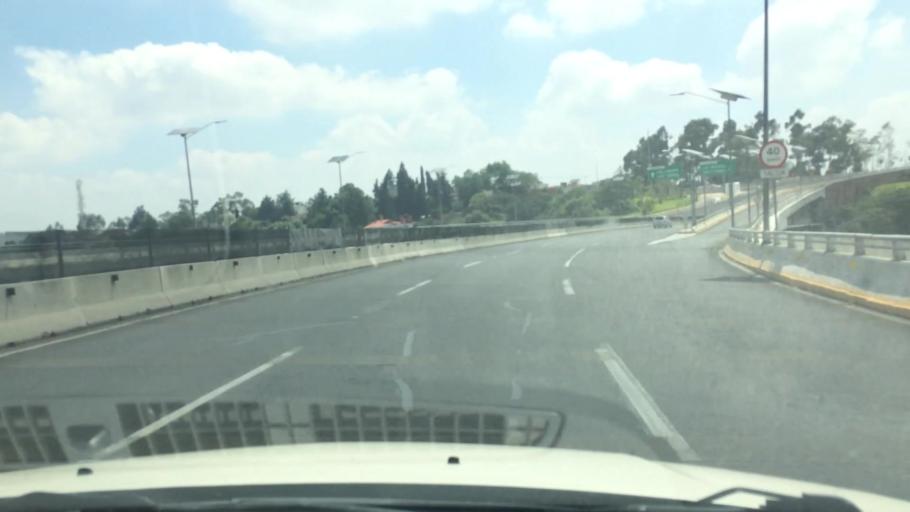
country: MX
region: Mexico City
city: Magdalena Contreras
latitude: 19.3464
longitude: -99.2414
